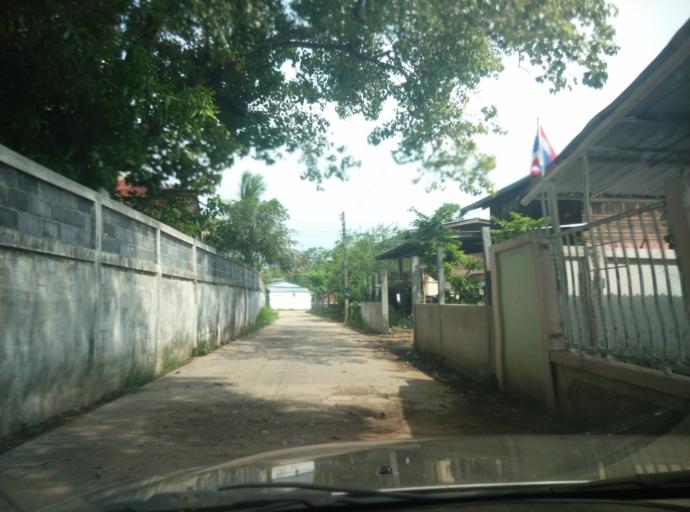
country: TH
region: Sisaket
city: Huai Thap Than
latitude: 15.0515
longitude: 104.0838
